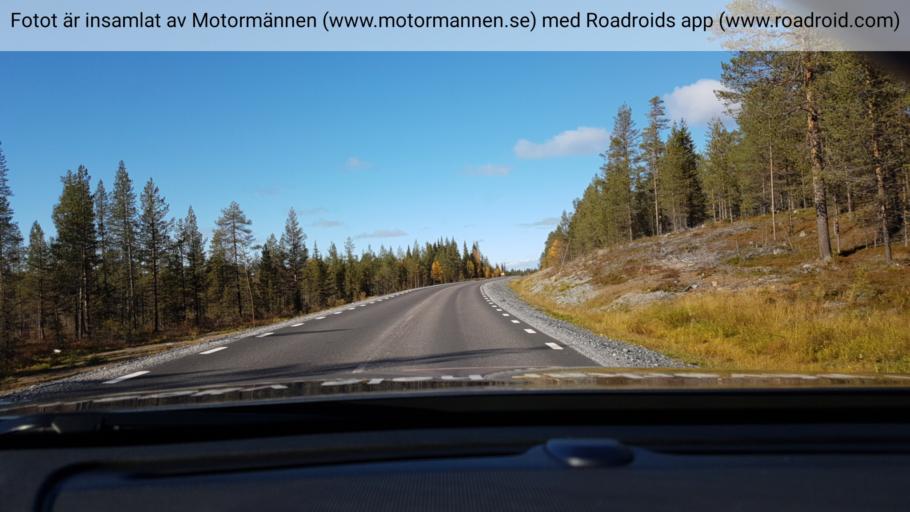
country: SE
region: Norrbotten
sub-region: Gallivare Kommun
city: Gaellivare
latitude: 66.9415
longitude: 20.8140
